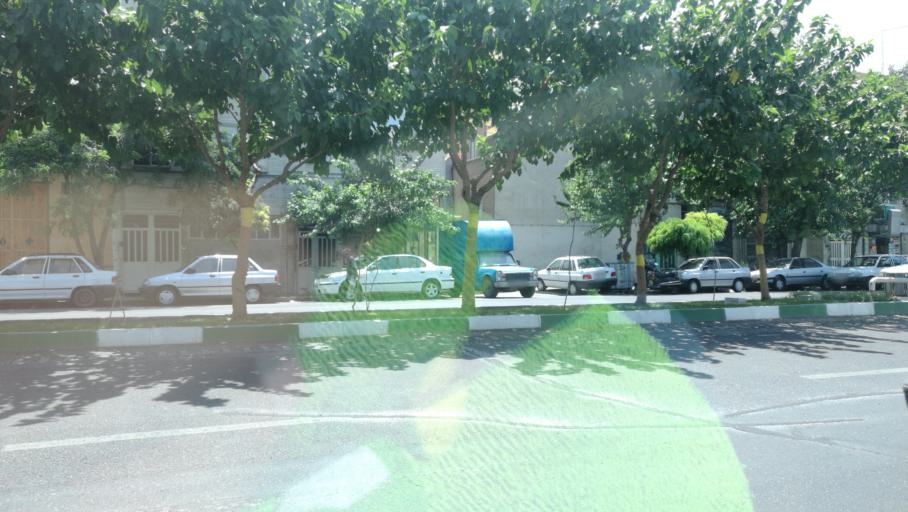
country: IR
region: Tehran
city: Tehran
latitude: 35.6867
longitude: 51.3568
